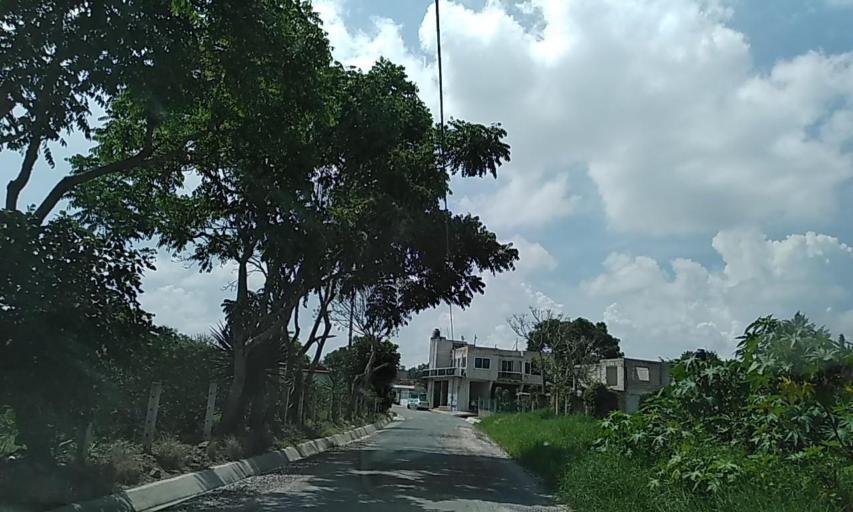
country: MX
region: Veracruz
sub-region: Emiliano Zapata
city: Dos Rios
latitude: 19.4426
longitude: -96.7807
